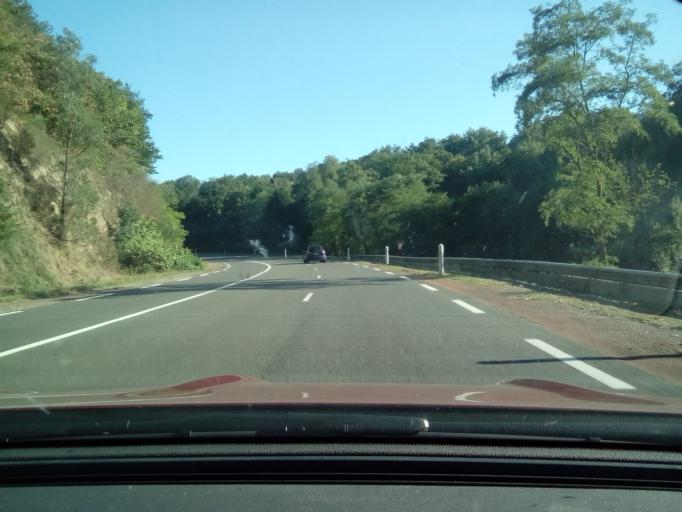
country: FR
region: Rhone-Alpes
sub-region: Departement du Rhone
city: Lissieu
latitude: 45.8481
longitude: 4.7187
